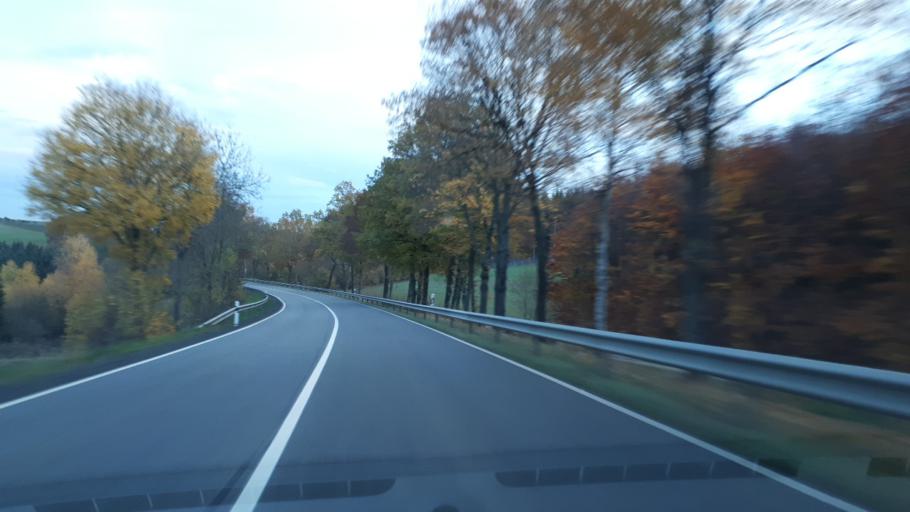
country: DE
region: Rheinland-Pfalz
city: Buchel
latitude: 50.1865
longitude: 7.0640
